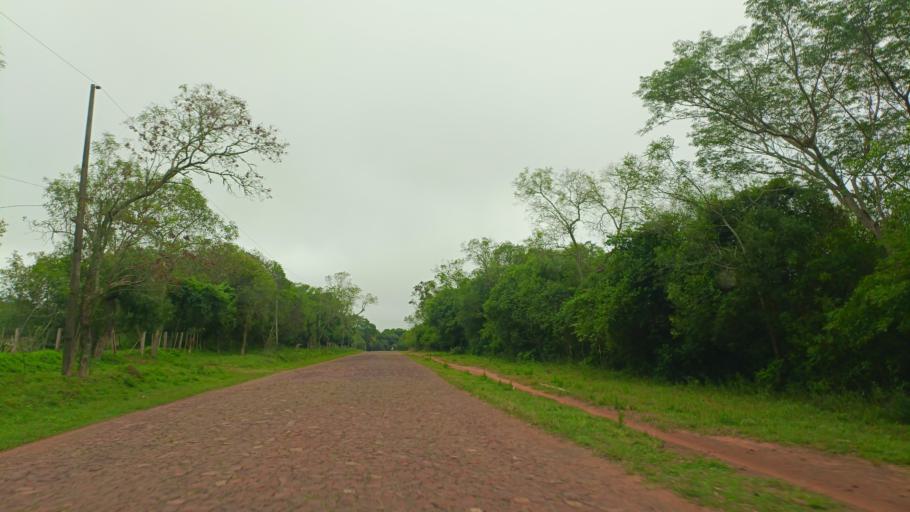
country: PY
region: Misiones
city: Santa Maria
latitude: -26.8668
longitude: -57.0112
